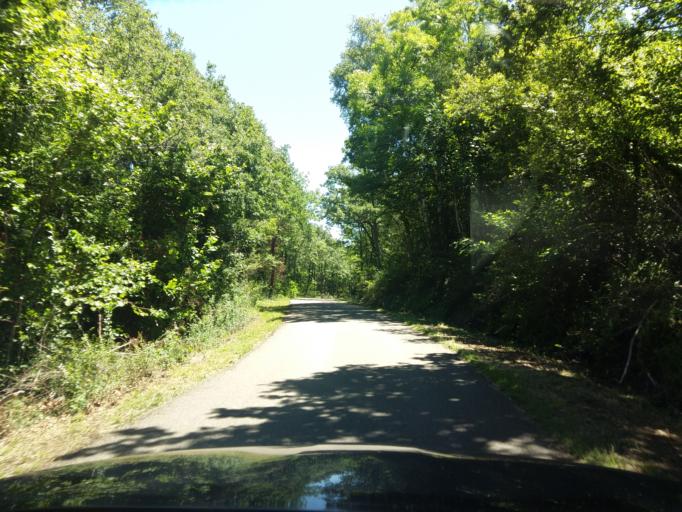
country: ES
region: Aragon
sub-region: Provincia de Zaragoza
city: Litago
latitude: 41.7985
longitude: -1.7888
